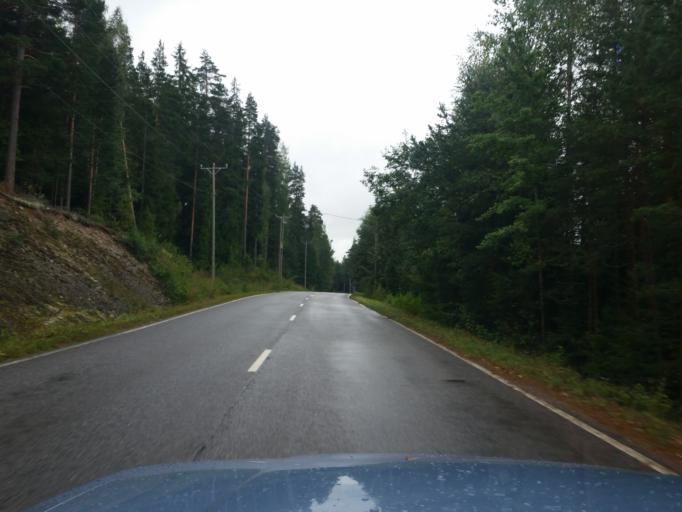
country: FI
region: Uusimaa
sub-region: Helsinki
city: Kaerkoelae
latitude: 60.5329
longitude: 23.9775
